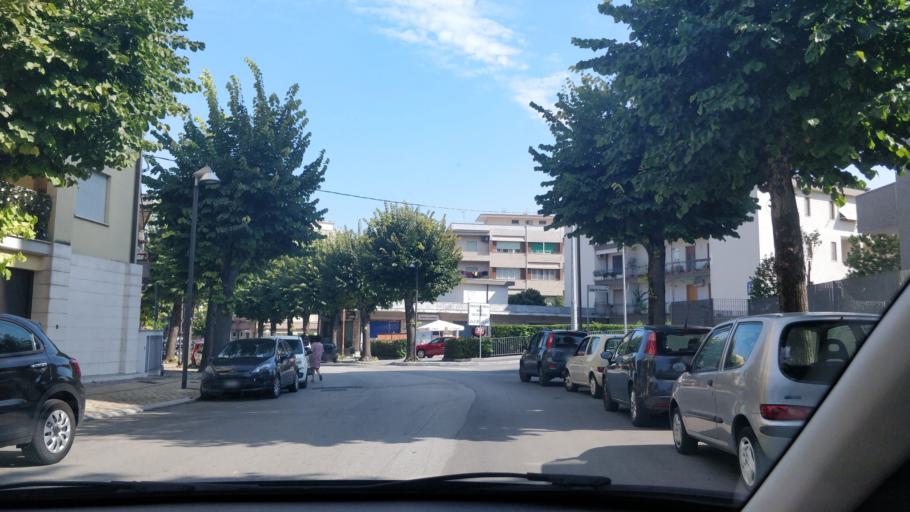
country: IT
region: Abruzzo
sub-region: Provincia di Chieti
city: Chieti
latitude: 42.3556
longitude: 14.1436
